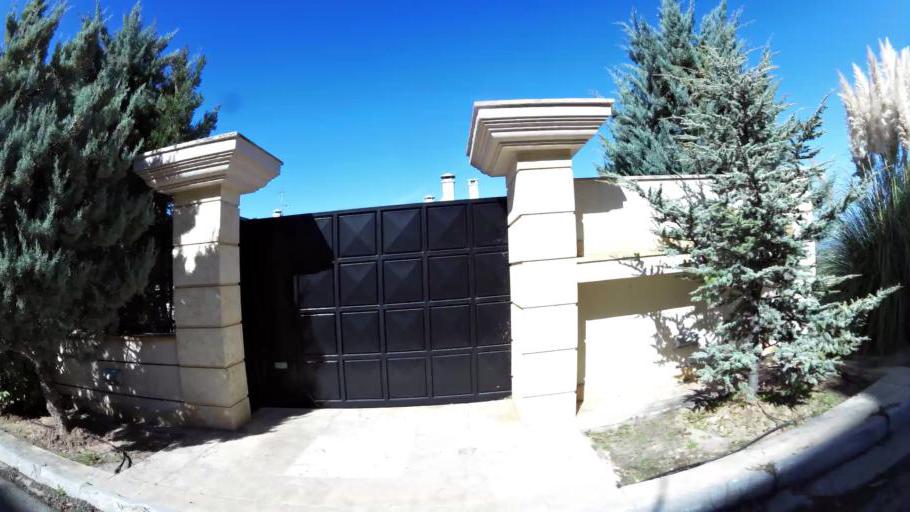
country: GR
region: Attica
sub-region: Nomarchia Anatolikis Attikis
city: Rodopoli
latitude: 38.1124
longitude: 23.8830
